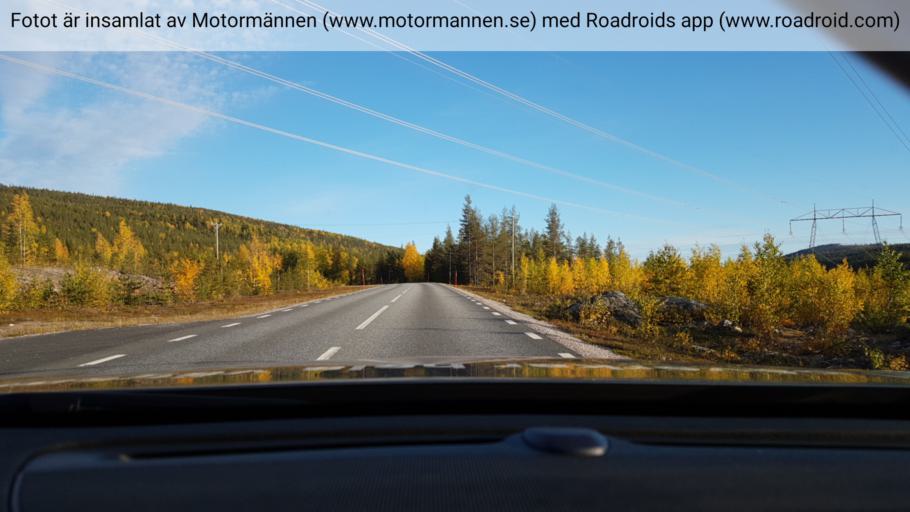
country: SE
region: Norrbotten
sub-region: Jokkmokks Kommun
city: Jokkmokk
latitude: 66.8499
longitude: 19.8237
